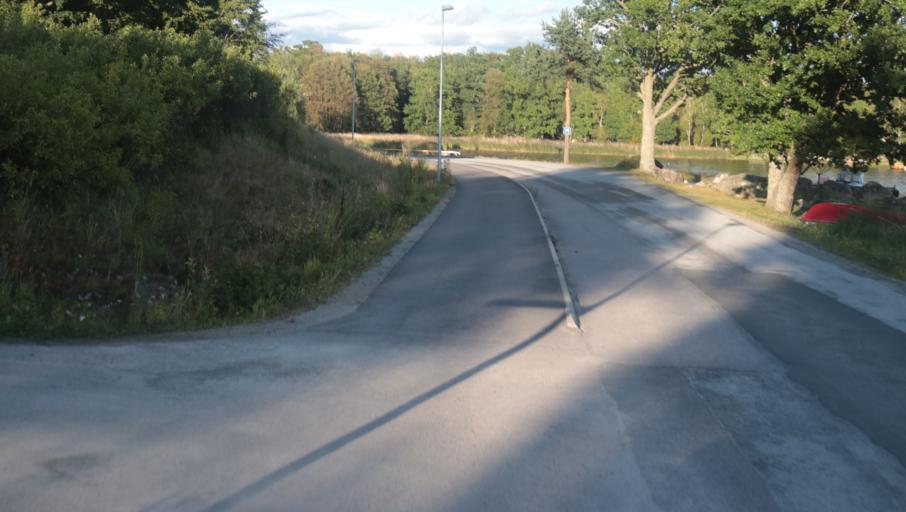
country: SE
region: Blekinge
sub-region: Karlshamns Kommun
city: Karlshamn
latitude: 56.1665
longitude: 14.9118
